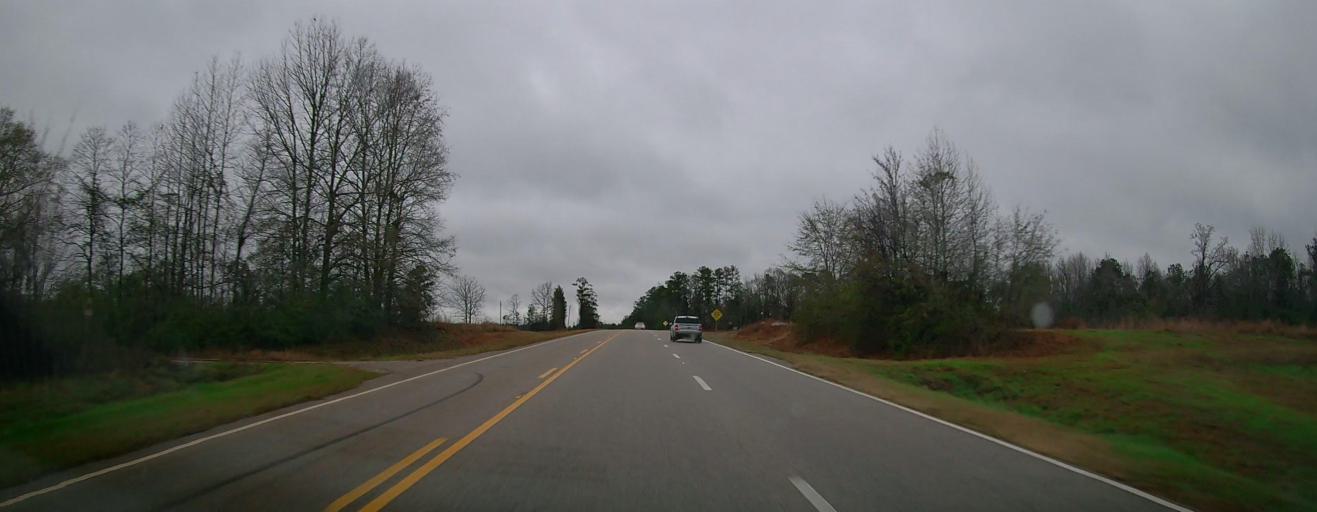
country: US
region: Alabama
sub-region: Bibb County
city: Centreville
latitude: 32.8575
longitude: -86.9657
